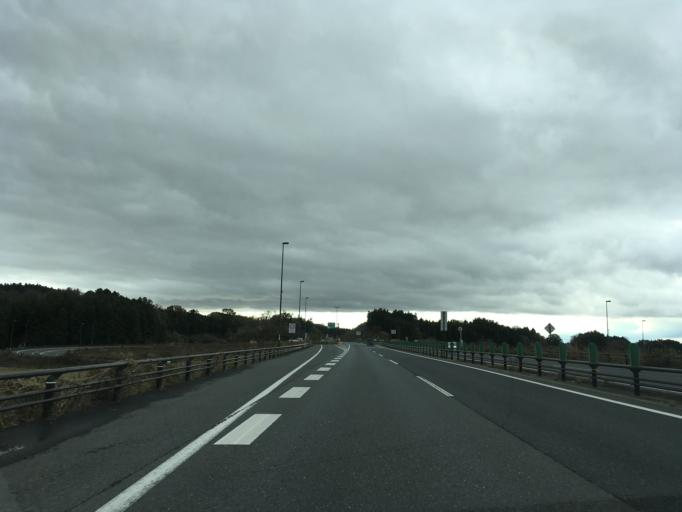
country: JP
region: Miyagi
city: Wakuya
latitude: 38.5632
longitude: 141.2717
